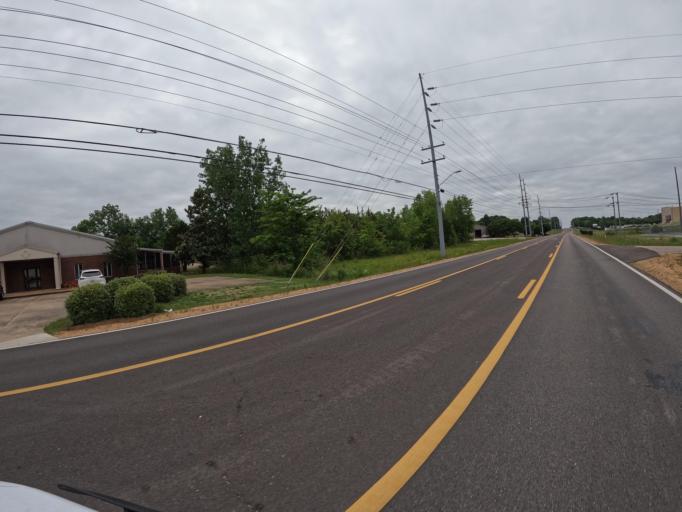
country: US
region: Mississippi
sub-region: Lee County
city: Tupelo
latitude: 34.2749
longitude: -88.7643
